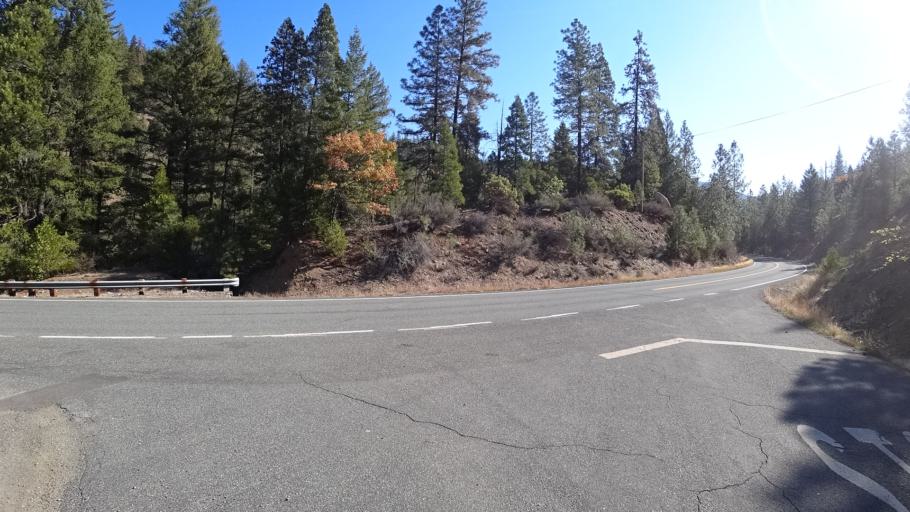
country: US
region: California
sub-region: Siskiyou County
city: Happy Camp
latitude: 41.7643
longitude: -123.0211
